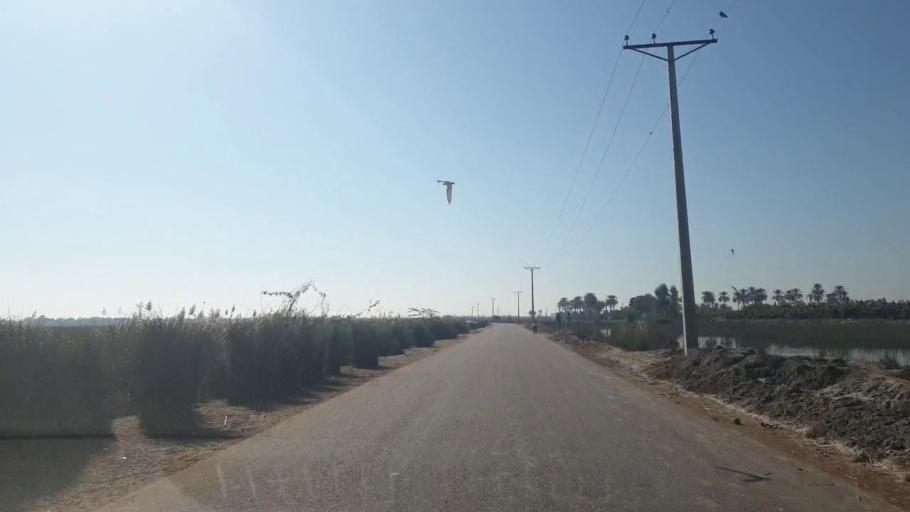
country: PK
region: Sindh
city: Kot Diji
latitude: 27.3180
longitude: 68.6495
